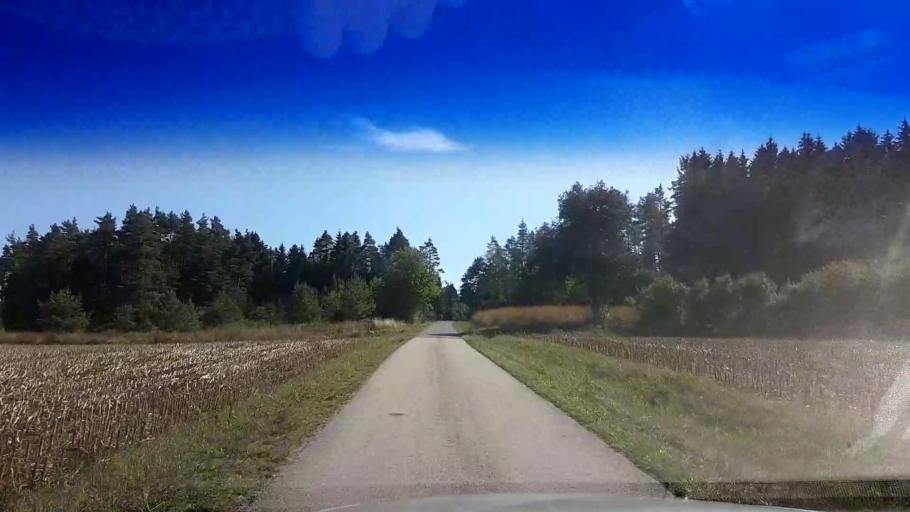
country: DE
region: Bavaria
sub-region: Upper Franconia
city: Poxdorf
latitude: 49.8816
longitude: 11.0886
